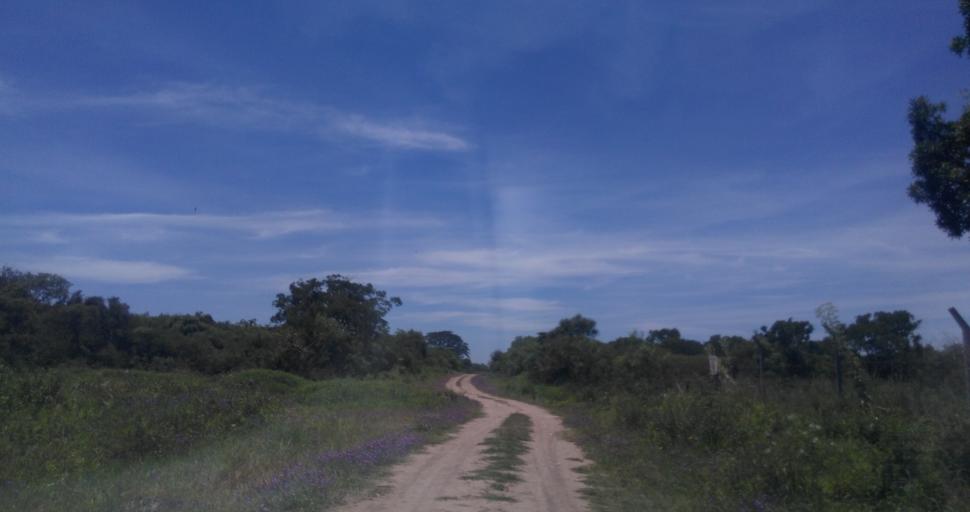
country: AR
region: Chaco
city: Fontana
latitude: -27.4280
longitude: -59.0484
